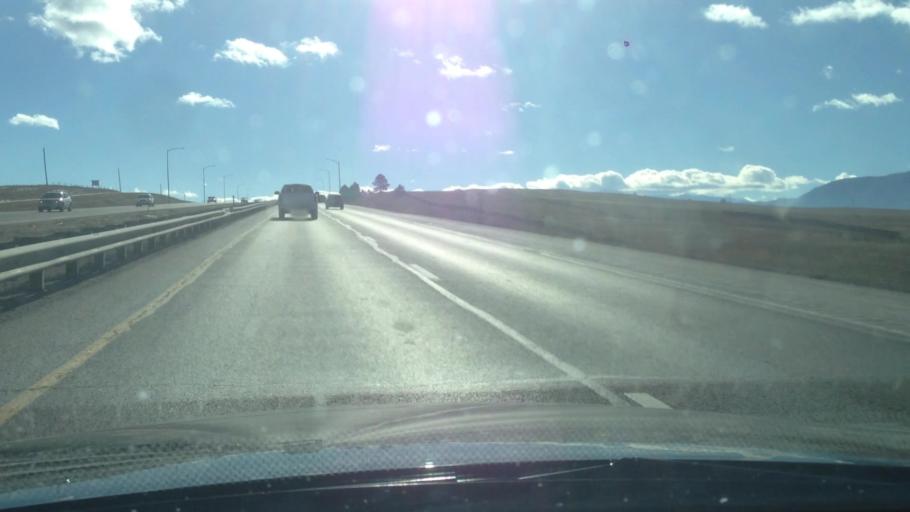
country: US
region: Colorado
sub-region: El Paso County
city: Woodmoor
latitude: 39.1382
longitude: -104.8626
